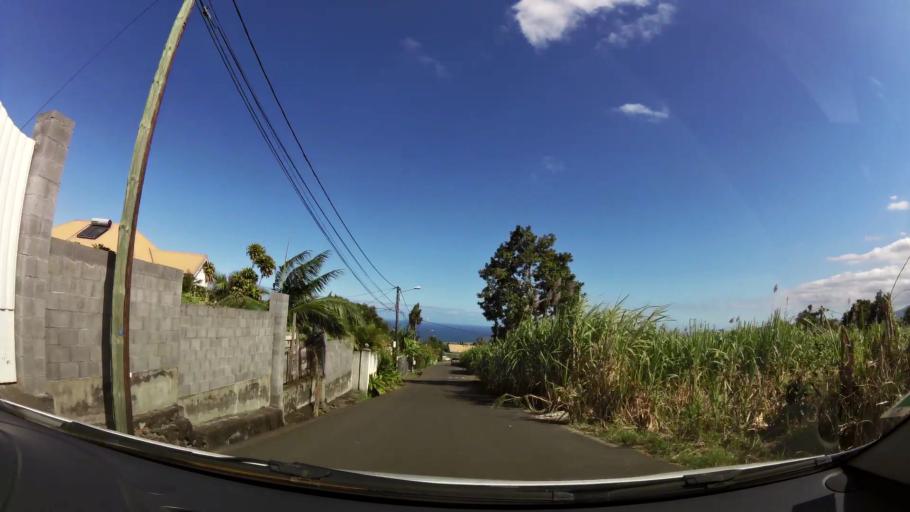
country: RE
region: Reunion
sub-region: Reunion
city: Le Tampon
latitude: -21.2897
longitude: 55.5052
